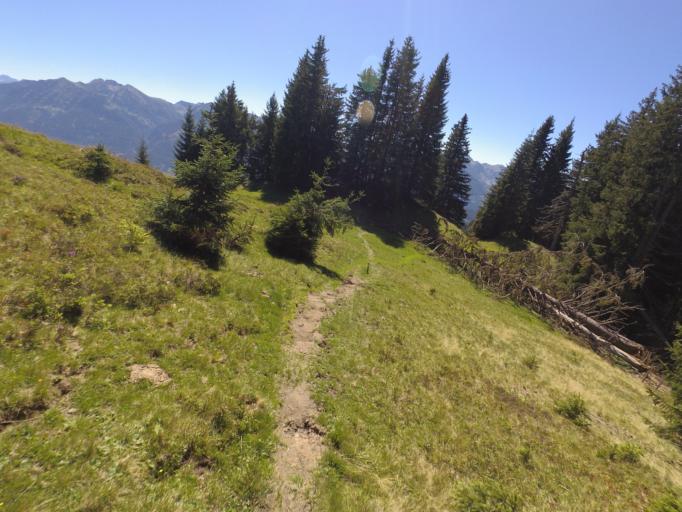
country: AT
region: Salzburg
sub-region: Politischer Bezirk Sankt Johann im Pongau
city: Goldegg
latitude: 47.3441
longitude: 13.0659
